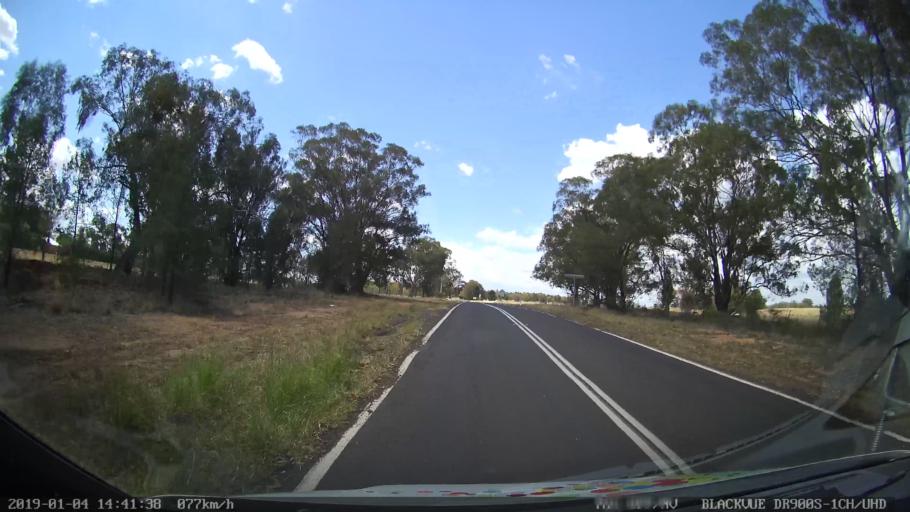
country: AU
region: New South Wales
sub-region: Dubbo Municipality
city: Dubbo
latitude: -32.1368
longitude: 148.6369
